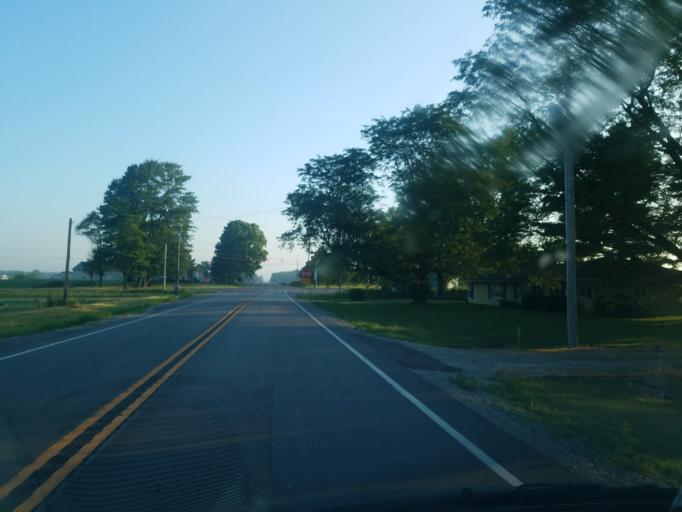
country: US
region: Indiana
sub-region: Allen County
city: Harlan
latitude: 41.2310
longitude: -84.8656
